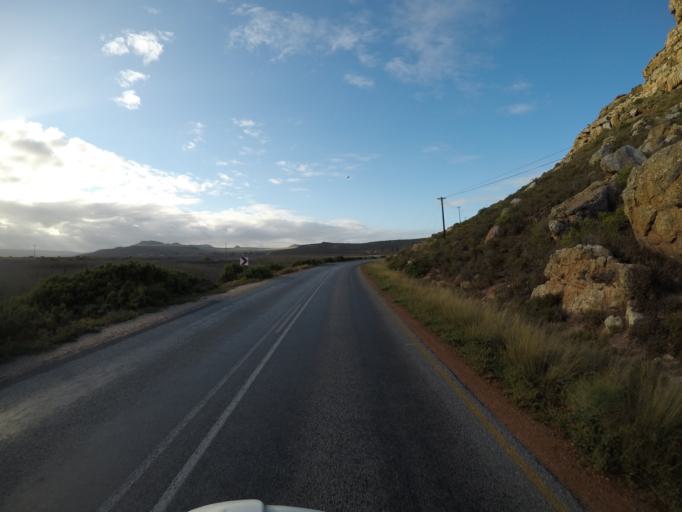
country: ZA
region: Western Cape
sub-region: West Coast District Municipality
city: Clanwilliam
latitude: -32.3163
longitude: 18.3573
